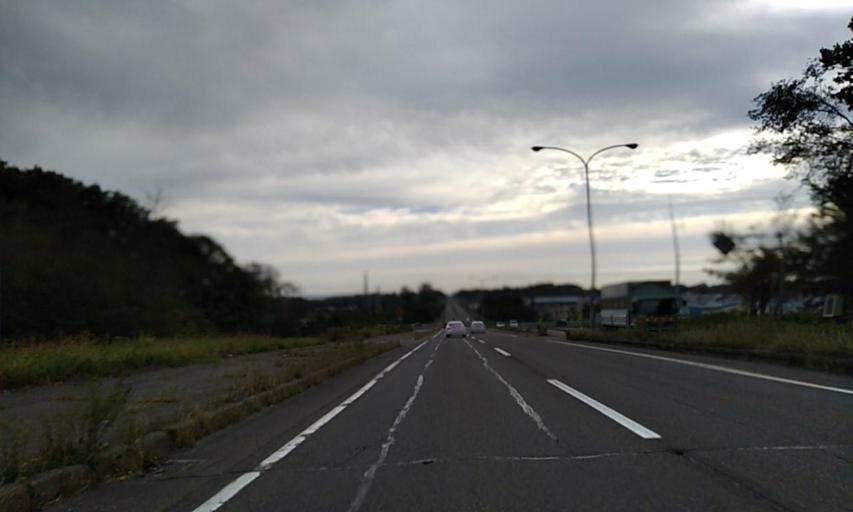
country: JP
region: Hokkaido
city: Obihiro
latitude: 42.9188
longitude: 143.0269
